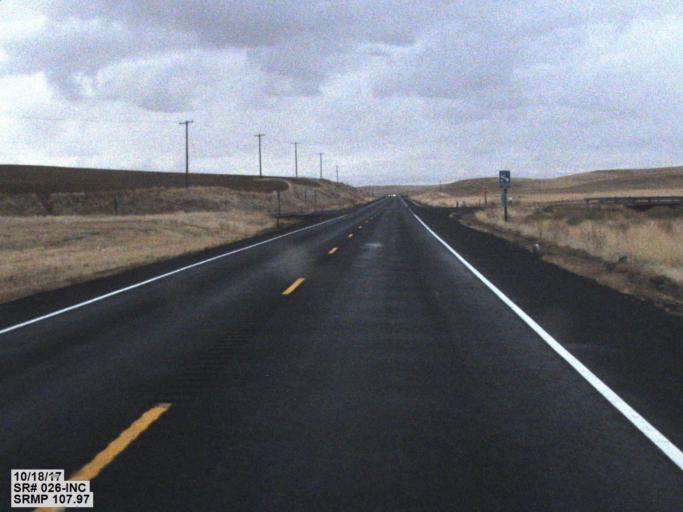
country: US
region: Washington
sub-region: Garfield County
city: Pomeroy
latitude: 46.8061
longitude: -117.8322
